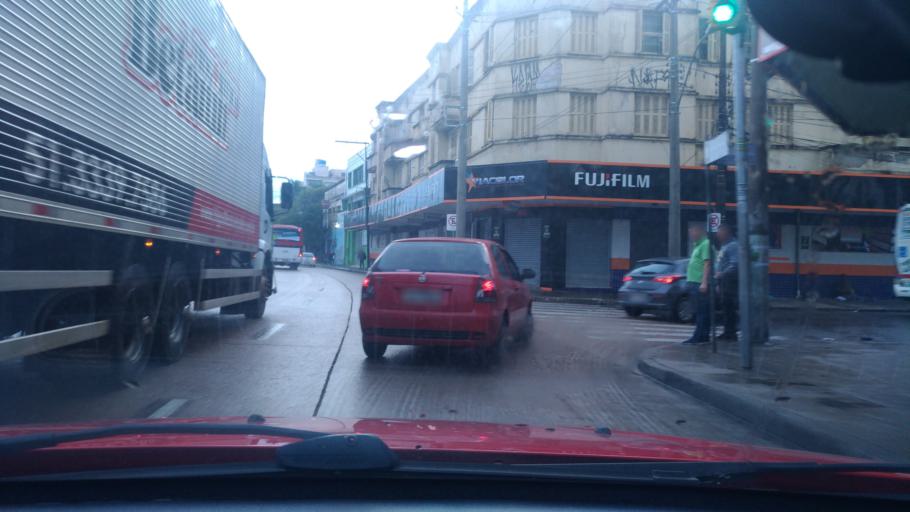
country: BR
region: Rio Grande do Sul
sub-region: Porto Alegre
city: Porto Alegre
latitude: -30.0214
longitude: -51.2114
